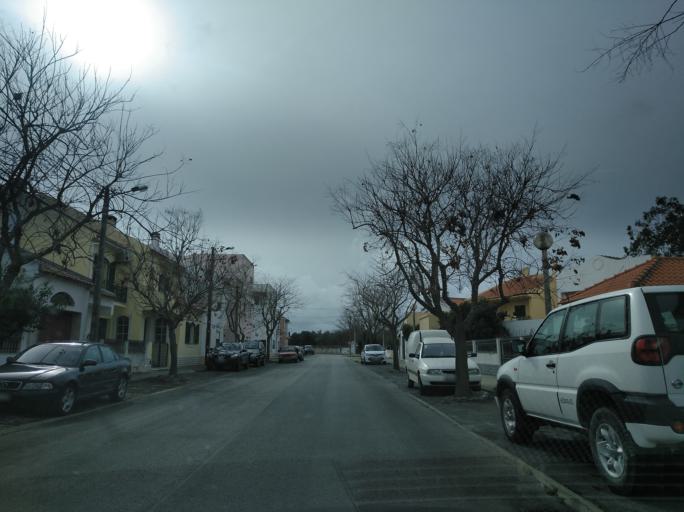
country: PT
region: Setubal
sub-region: Grandola
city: Grandola
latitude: 38.1799
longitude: -8.5641
